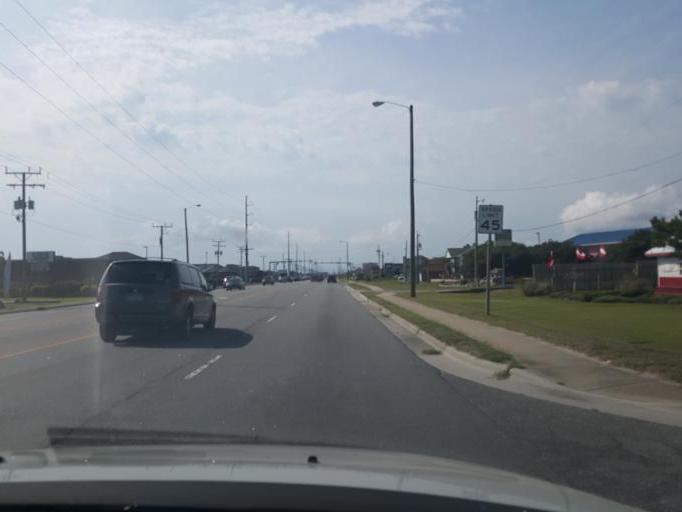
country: US
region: North Carolina
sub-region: Dare County
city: Kill Devil Hills
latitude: 36.0065
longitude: -75.6567
